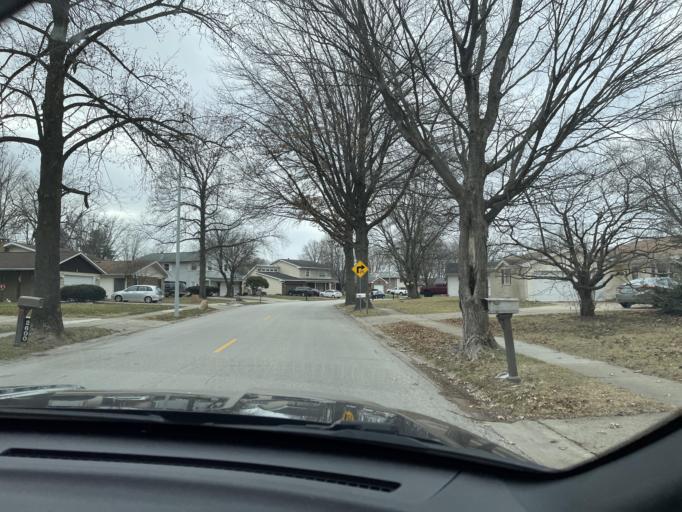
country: US
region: Illinois
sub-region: Sangamon County
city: Leland Grove
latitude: 39.7957
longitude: -89.7003
